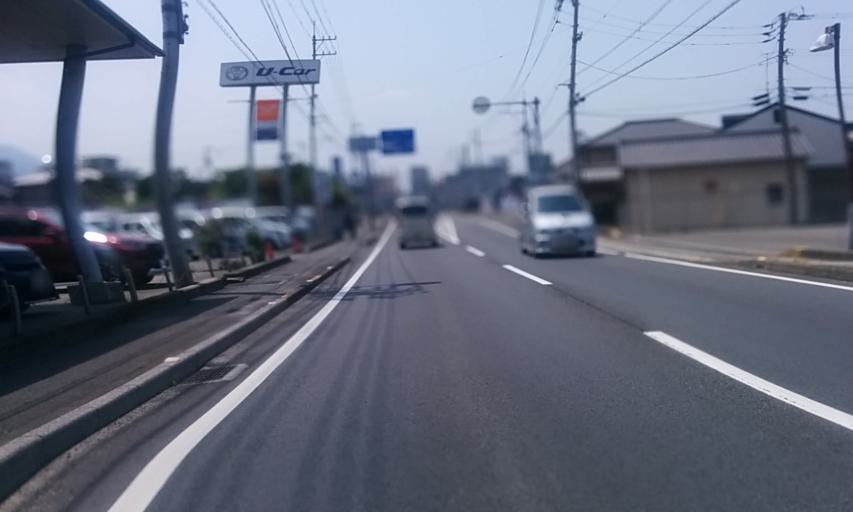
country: JP
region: Ehime
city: Niihama
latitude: 33.9325
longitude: 133.2863
